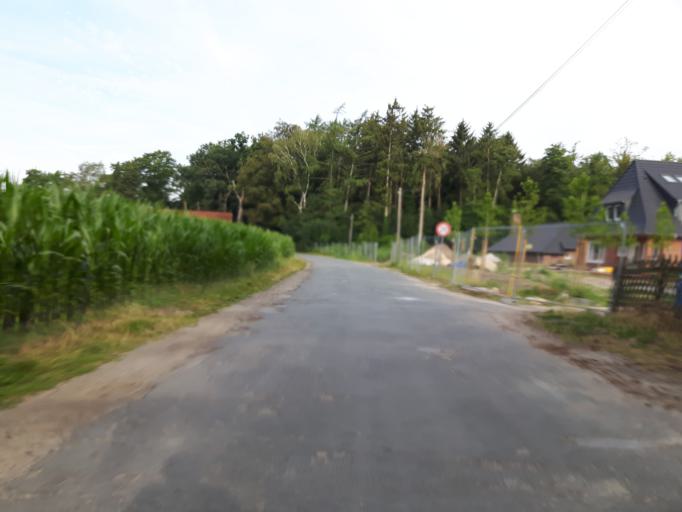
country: DE
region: Lower Saxony
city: Delmenhorst
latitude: 53.0815
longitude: 8.6410
